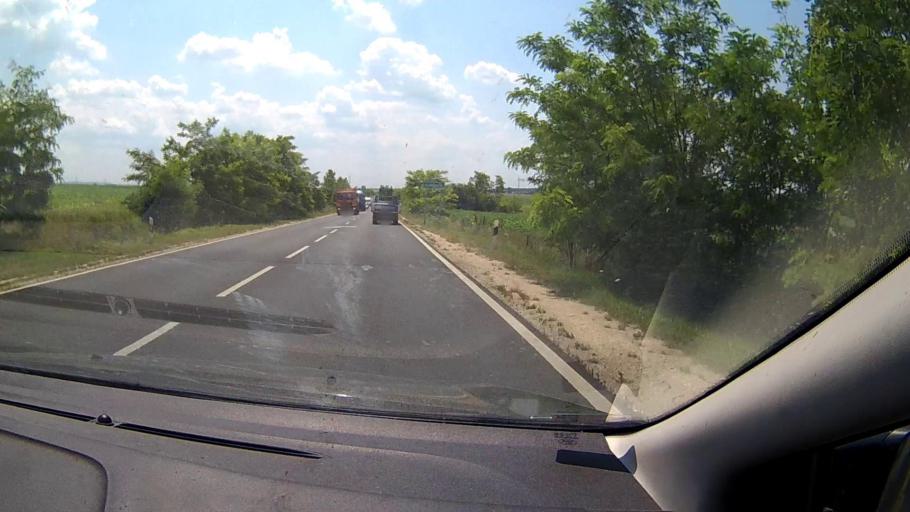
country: HU
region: Komarom-Esztergom
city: Tata
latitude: 47.6215
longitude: 18.3159
